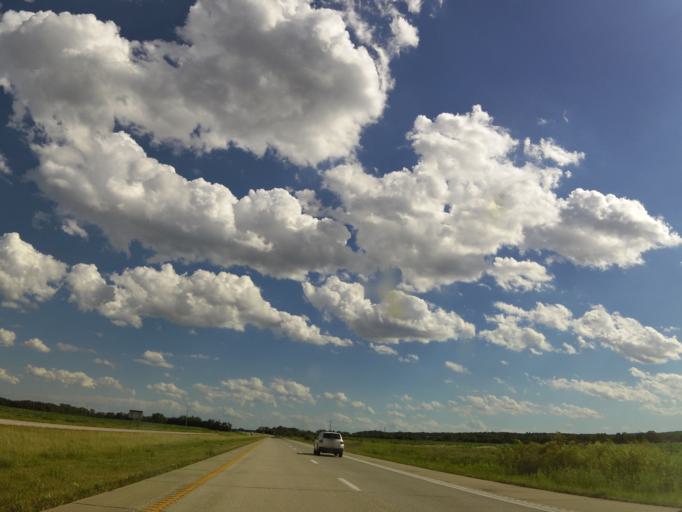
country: US
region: Missouri
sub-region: Clark County
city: Kahoka
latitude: 40.4276
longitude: -91.5711
